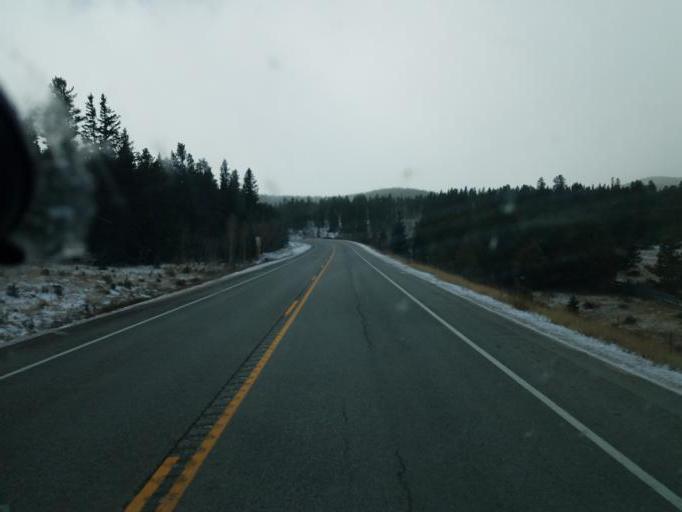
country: US
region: Colorado
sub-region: Clear Creek County
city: Georgetown
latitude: 39.4324
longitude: -105.7604
